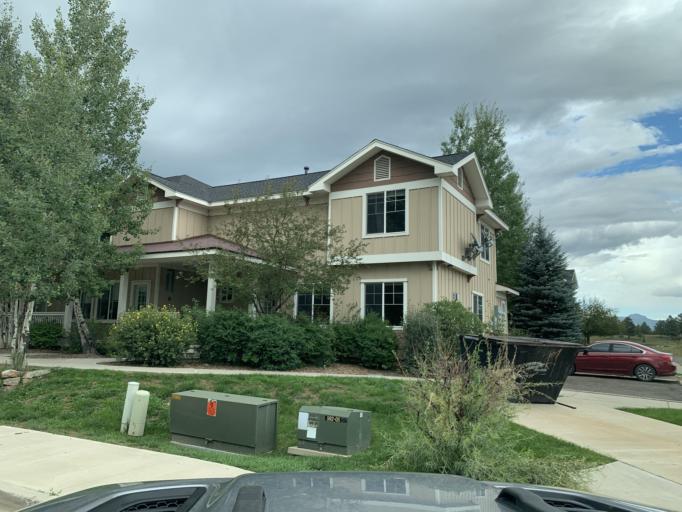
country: US
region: Colorado
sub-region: Archuleta County
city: Pagosa Springs
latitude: 37.2583
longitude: -107.0642
